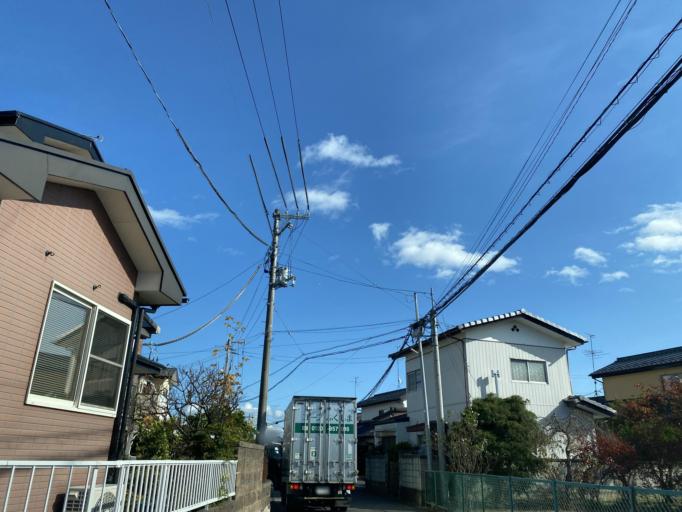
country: JP
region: Fukushima
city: Koriyama
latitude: 37.3870
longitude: 140.3373
